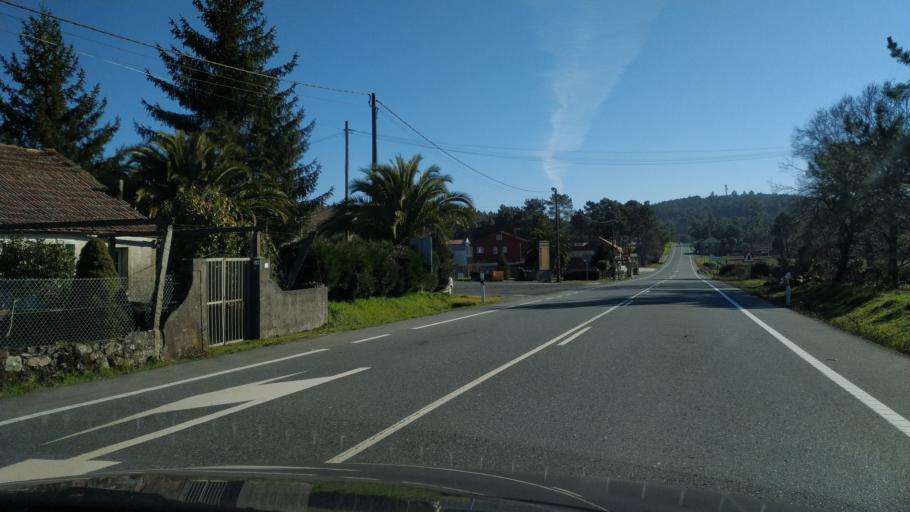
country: ES
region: Galicia
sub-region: Provincia da Coruna
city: Ribeira
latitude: 42.7564
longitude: -8.3621
